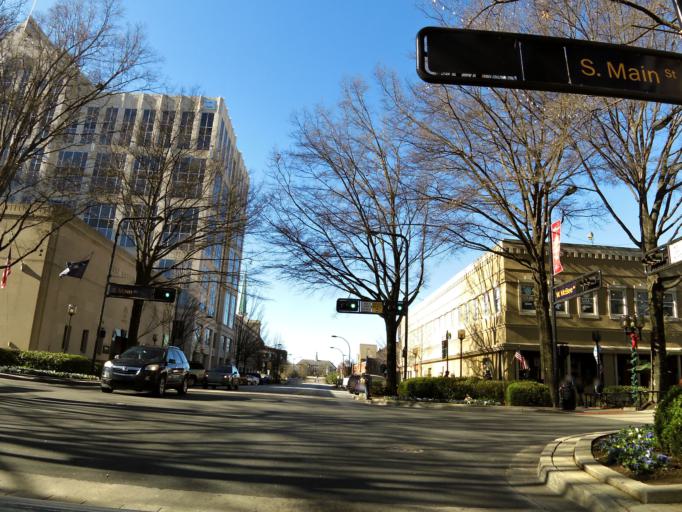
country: US
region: South Carolina
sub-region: Greenville County
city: Greenville
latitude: 34.8496
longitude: -82.3993
